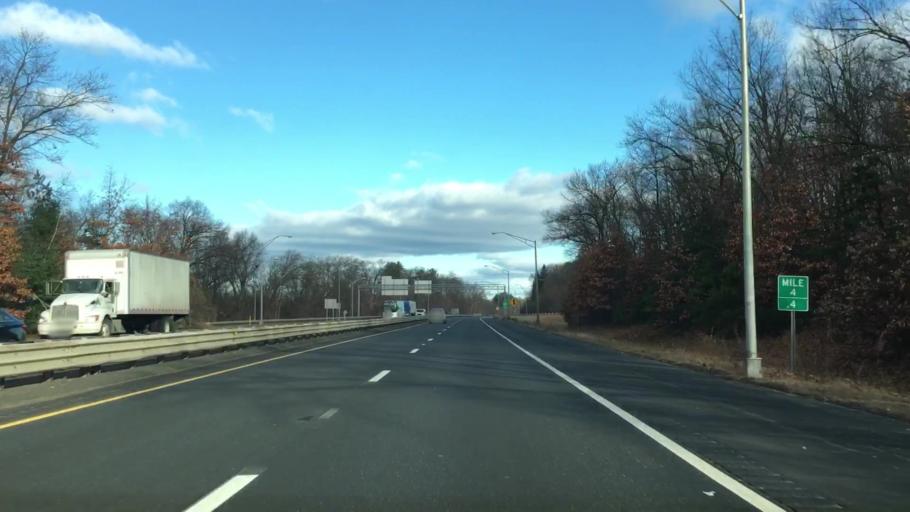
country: US
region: Massachusetts
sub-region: Hampden County
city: Chicopee
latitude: 42.1480
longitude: -72.5494
